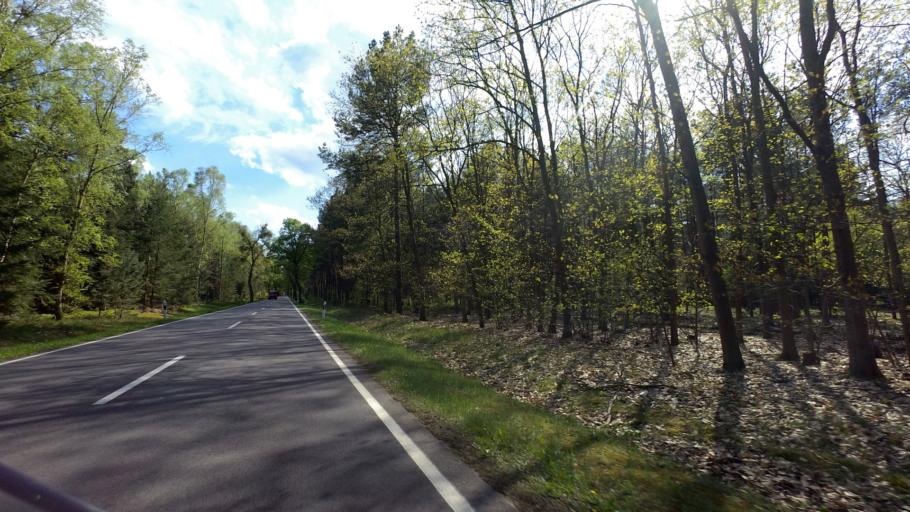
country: DE
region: Brandenburg
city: Milmersdorf
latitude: 53.0246
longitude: 13.6034
